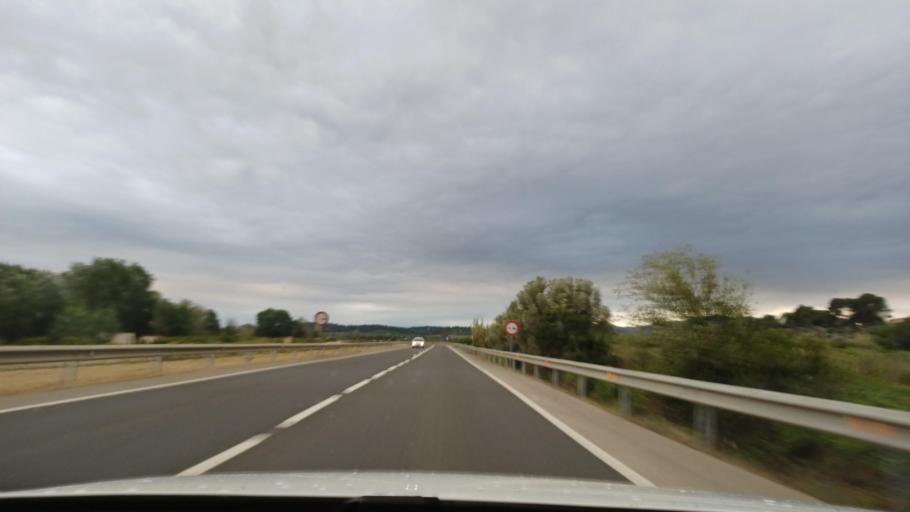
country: ES
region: Catalonia
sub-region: Provincia de Tarragona
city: Masdenverge
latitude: 40.7617
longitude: 0.5340
